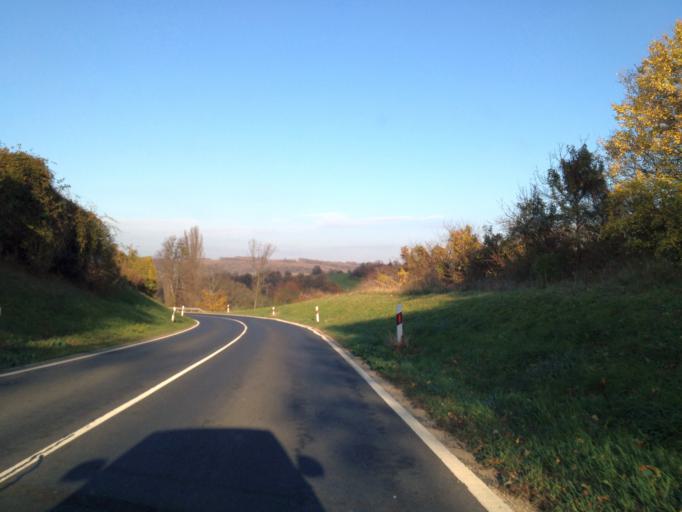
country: HU
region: Gyor-Moson-Sopron
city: Bakonyszentlaszlo
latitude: 47.3570
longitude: 17.8717
